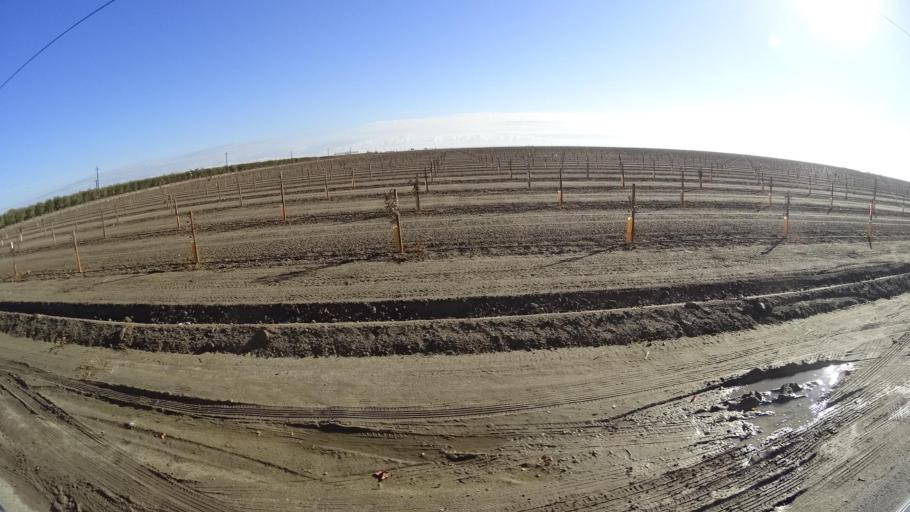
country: US
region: California
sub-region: Kern County
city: Delano
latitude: 35.7167
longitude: -119.3118
